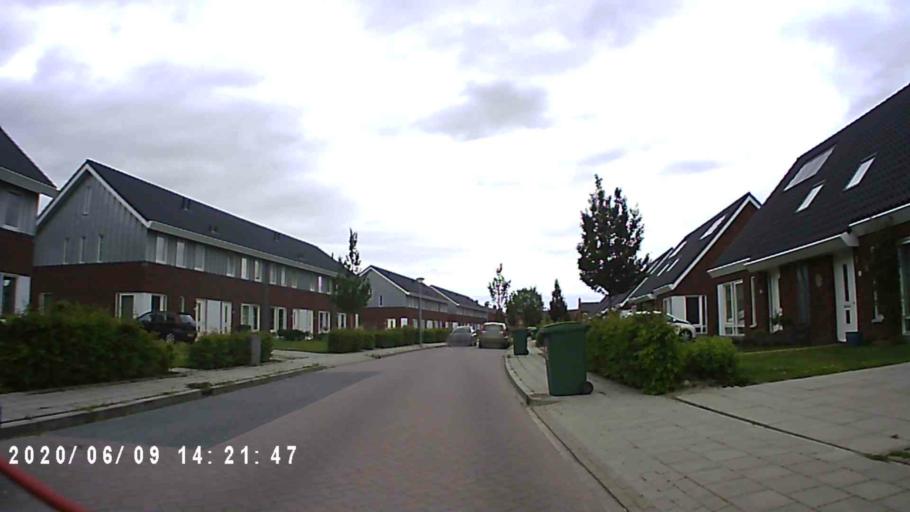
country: NL
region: Groningen
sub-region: Gemeente Bedum
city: Bedum
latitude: 53.2981
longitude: 6.5923
